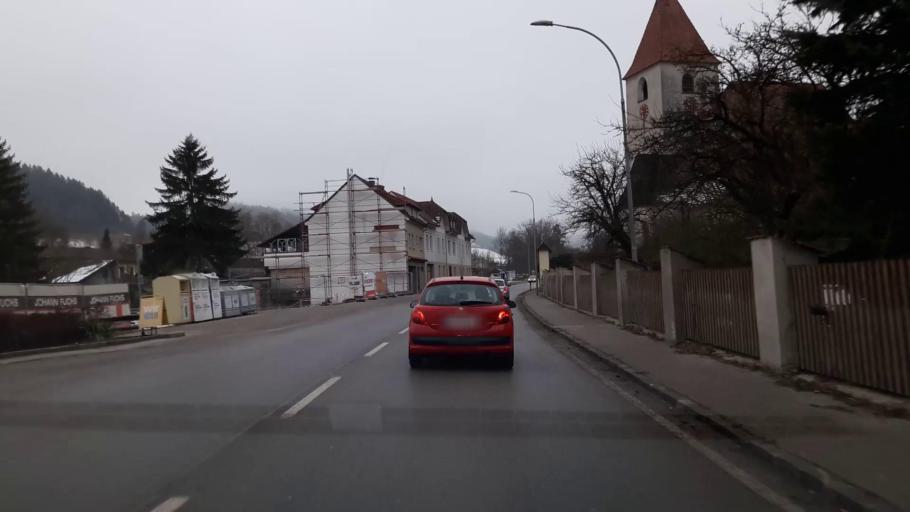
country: AT
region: Lower Austria
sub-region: Politischer Bezirk Neunkirchen
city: Thomasberg
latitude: 47.5714
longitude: 16.0995
